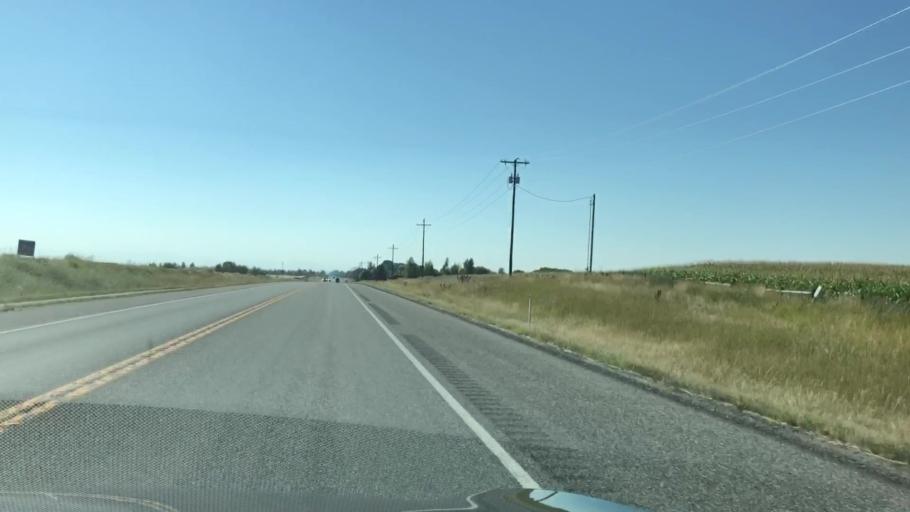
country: US
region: Montana
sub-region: Gallatin County
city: Belgrade
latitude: 45.7291
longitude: -111.1075
